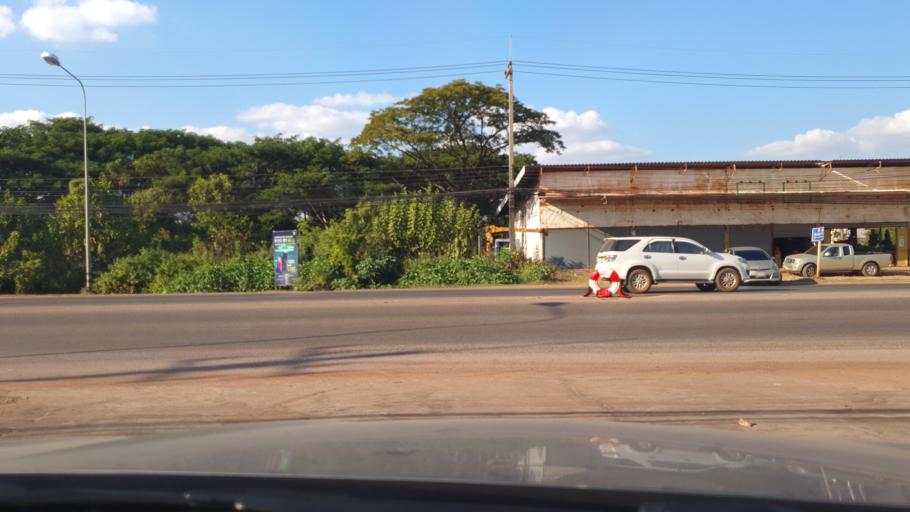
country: TH
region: Sakon Nakhon
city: Sakon Nakhon
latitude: 17.1470
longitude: 104.1278
